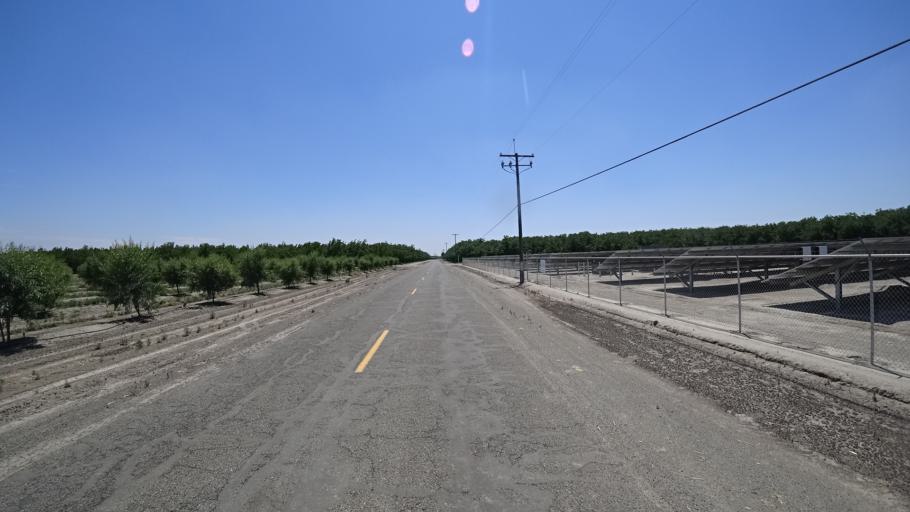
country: US
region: California
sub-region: Kings County
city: Lucerne
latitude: 36.4060
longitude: -119.6189
